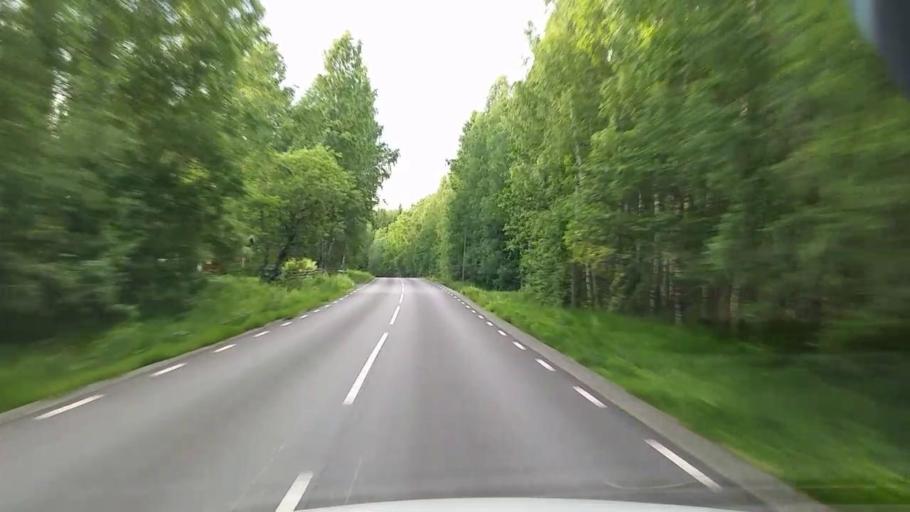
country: SE
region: Vaestmanland
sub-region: Kopings Kommun
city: Kolsva
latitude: 59.7224
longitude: 15.8331
